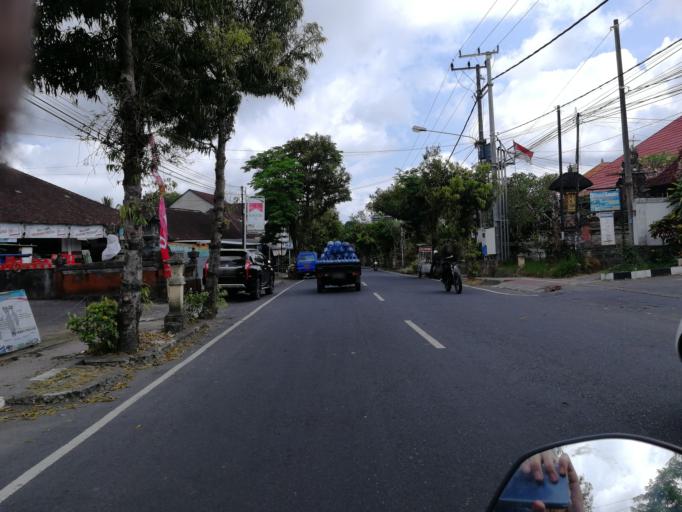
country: ID
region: Bali
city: Banjar Bebalang
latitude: -8.4669
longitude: 115.3526
